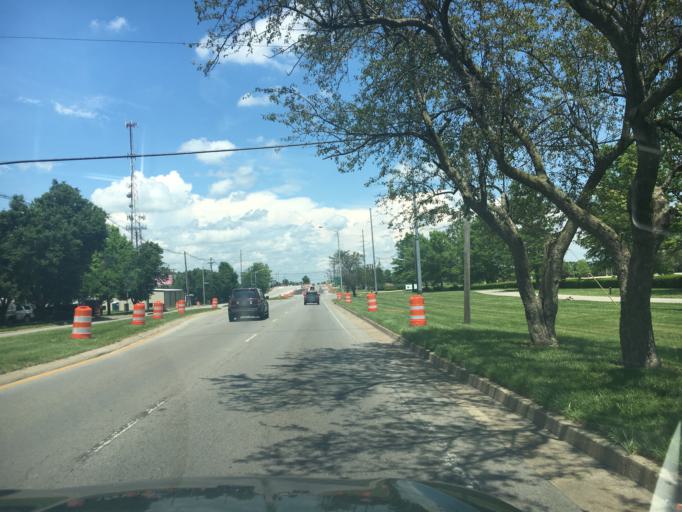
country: US
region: Kentucky
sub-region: Fayette County
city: Lexington-Fayette
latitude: 38.0701
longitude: -84.4970
